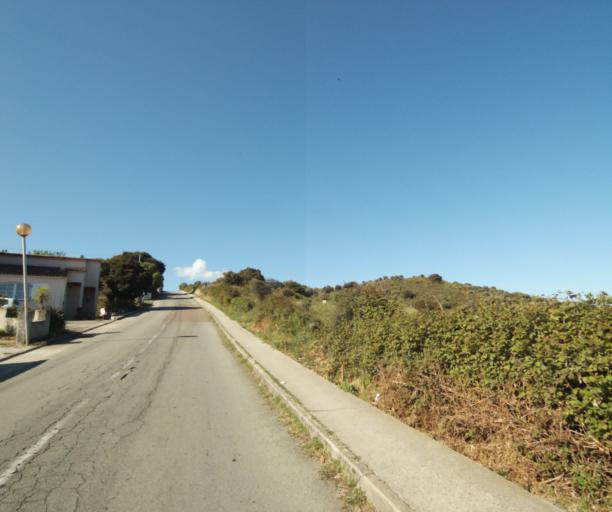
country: FR
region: Corsica
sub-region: Departement de la Corse-du-Sud
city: Propriano
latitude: 41.6716
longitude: 8.8986
